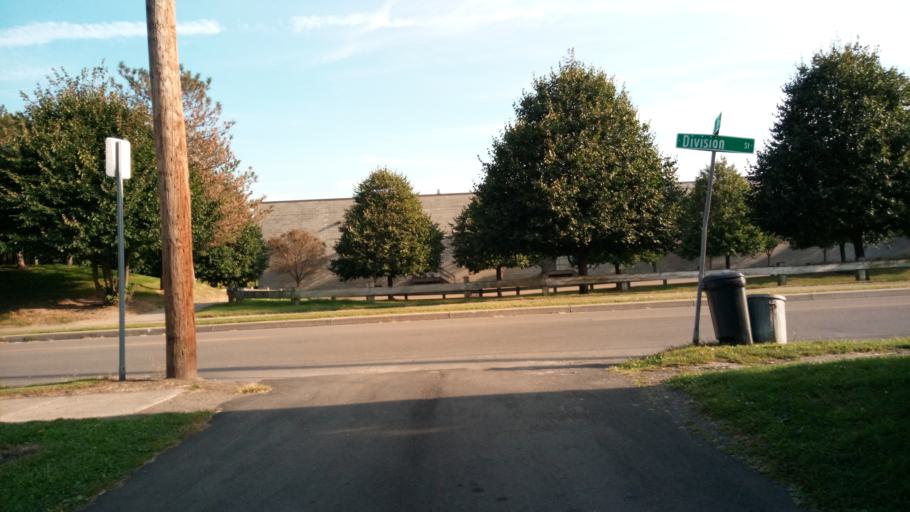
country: US
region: New York
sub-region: Chemung County
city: Elmira
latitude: 42.1071
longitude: -76.8091
